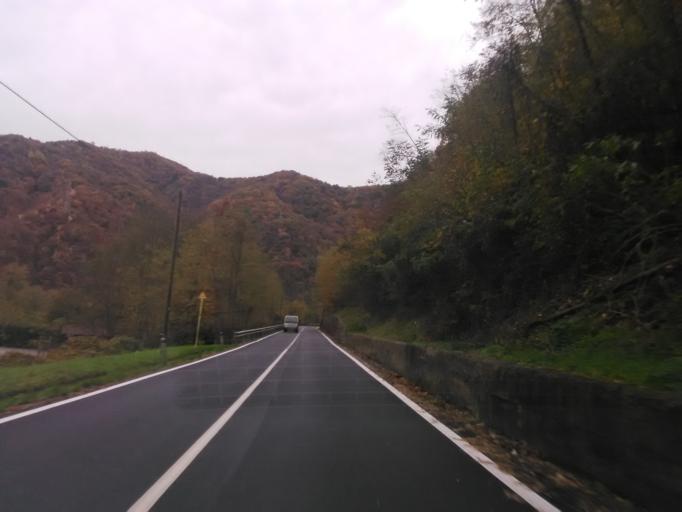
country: IT
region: Piedmont
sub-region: Provincia di Vercelli
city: Guardabosone
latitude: 45.6930
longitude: 8.2638
